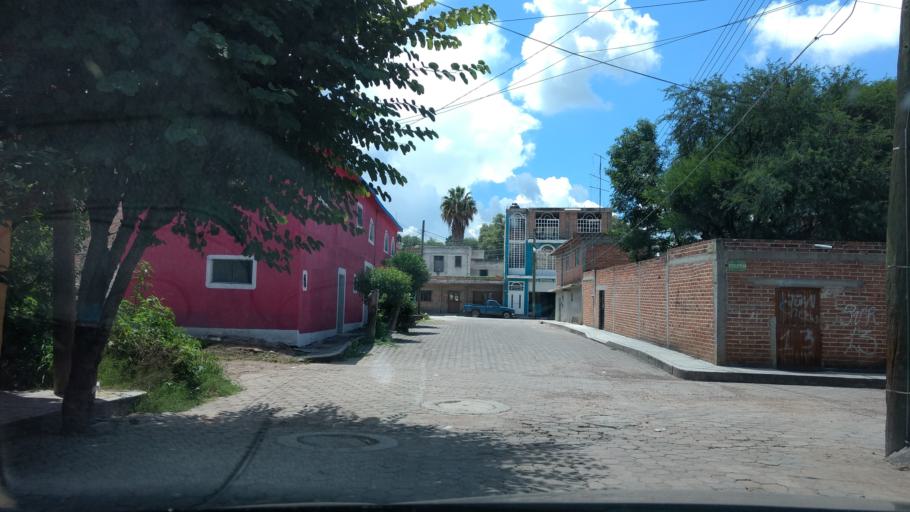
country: MX
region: Zacatecas
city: Tlaltenango de Sanchez Roman
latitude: 21.7789
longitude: -103.3002
